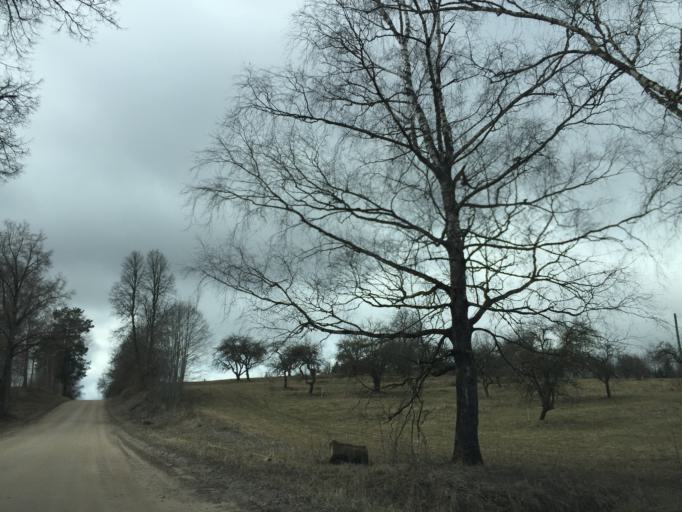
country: LV
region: Ilukste
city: Ilukste
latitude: 56.0663
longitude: 26.1135
